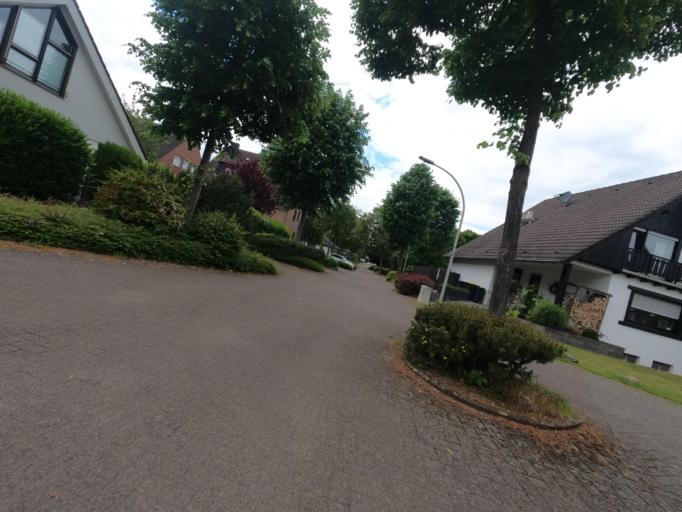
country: DE
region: North Rhine-Westphalia
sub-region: Regierungsbezirk Koln
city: Ubach-Palenberg
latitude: 50.9135
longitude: 6.1333
